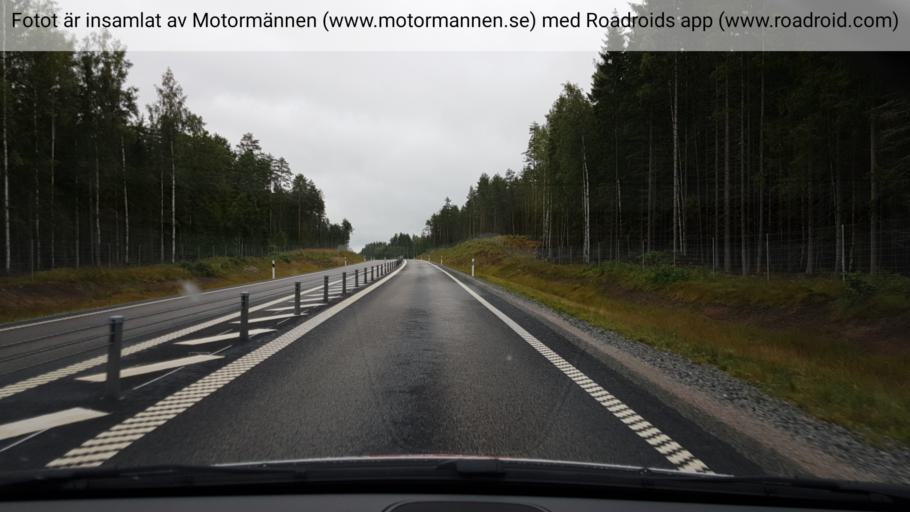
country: SE
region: Uppsala
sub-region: Heby Kommun
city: Tarnsjo
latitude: 60.0510
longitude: 16.8882
